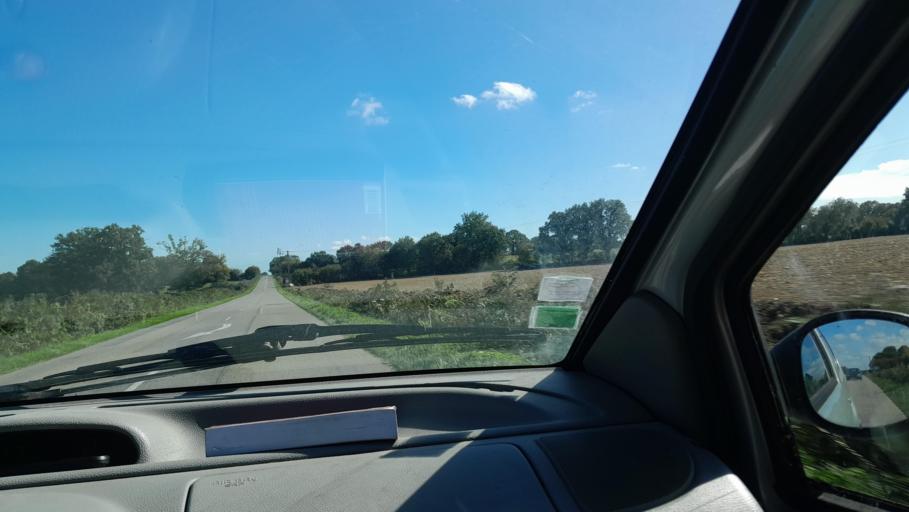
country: FR
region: Pays de la Loire
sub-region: Departement de la Mayenne
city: Cosse-le-Vivien
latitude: 47.9423
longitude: -0.8866
